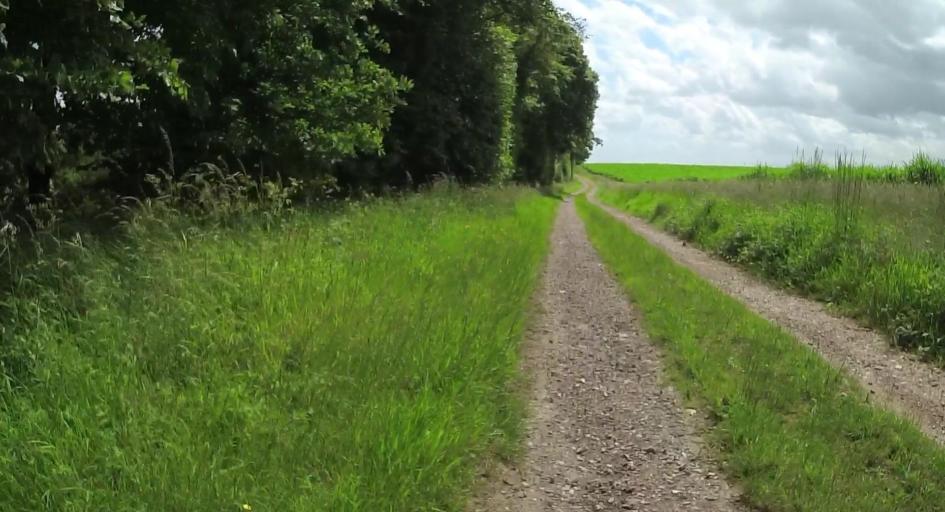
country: GB
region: England
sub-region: Hampshire
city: Basingstoke
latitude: 51.1833
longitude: -1.1641
